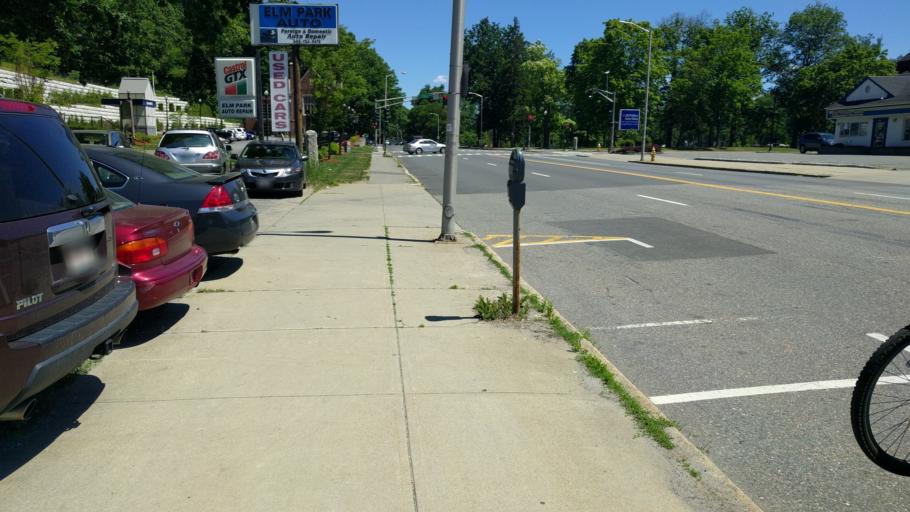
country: US
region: Massachusetts
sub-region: Worcester County
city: Worcester
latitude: 42.2658
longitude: -71.8187
